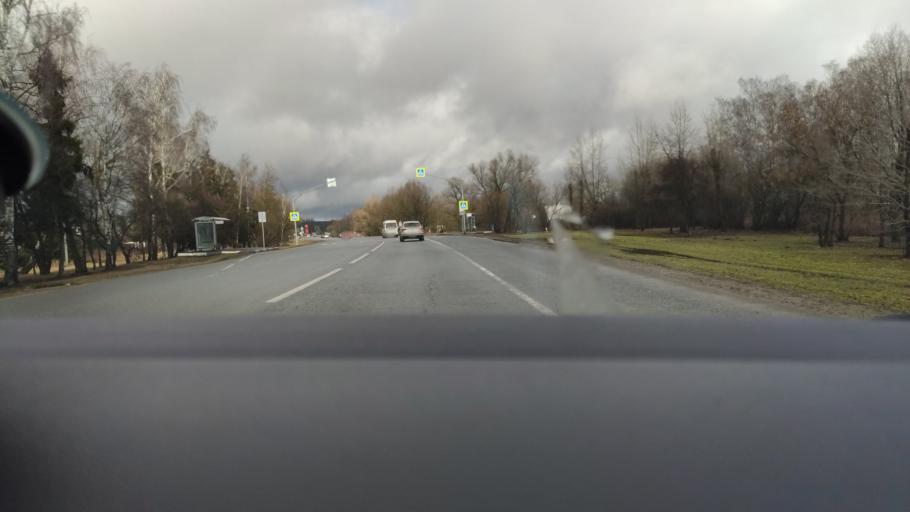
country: RU
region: Moskovskaya
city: Troitsk
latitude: 55.3374
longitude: 37.1713
